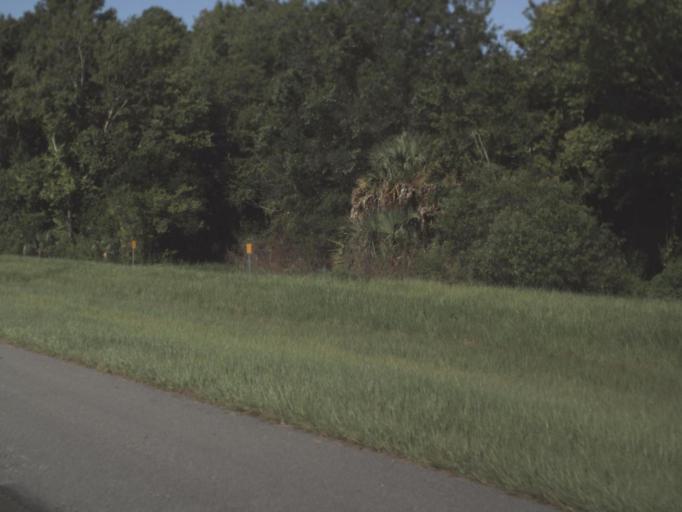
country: US
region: Florida
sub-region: Hillsborough County
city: Lutz
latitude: 28.1232
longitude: -82.4195
